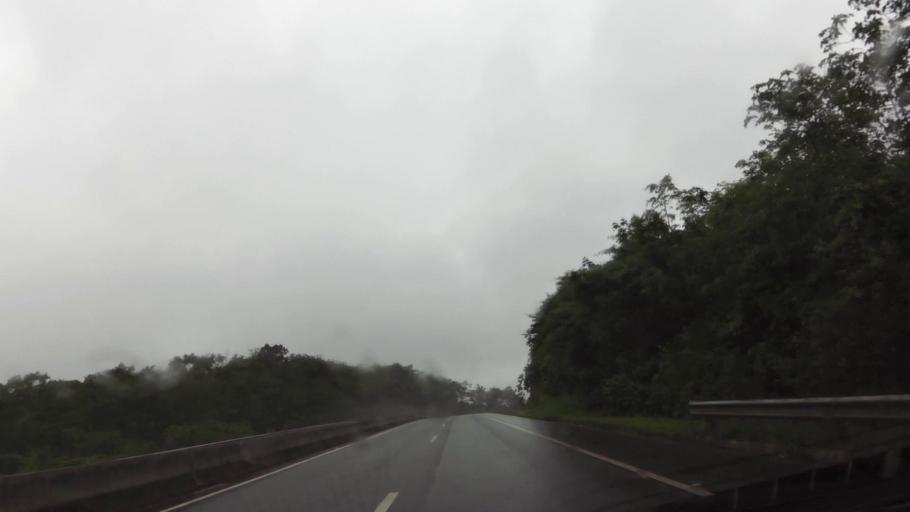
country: BR
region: Espirito Santo
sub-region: Guarapari
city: Guarapari
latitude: -20.6292
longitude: -40.5079
